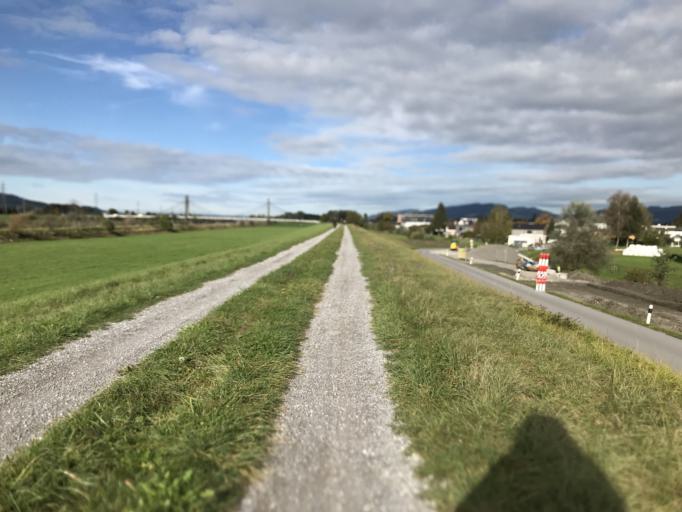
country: CH
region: Saint Gallen
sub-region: Wahlkreis Rheintal
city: Diepoldsau
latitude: 47.3842
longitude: 9.6444
